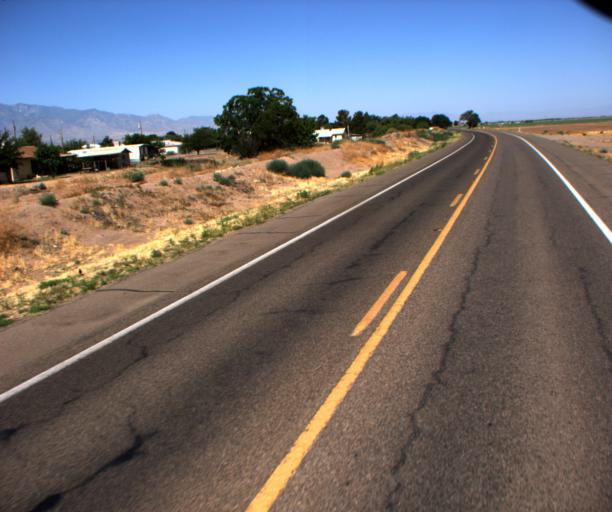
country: US
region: Arizona
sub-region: Graham County
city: Safford
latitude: 32.8158
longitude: -109.6270
